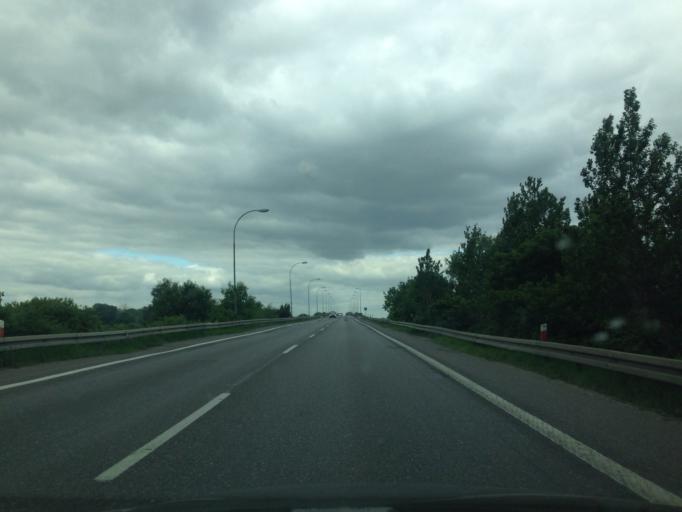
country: PL
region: Kujawsko-Pomorskie
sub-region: Powiat chelminski
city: Chelmno
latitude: 53.3648
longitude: 18.4330
